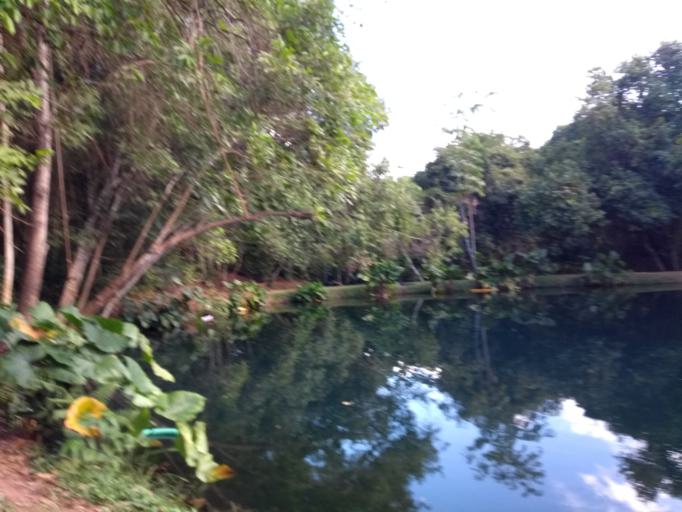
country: BR
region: Goias
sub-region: Goianesia
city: Goianesia
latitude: -15.5111
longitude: -48.9534
